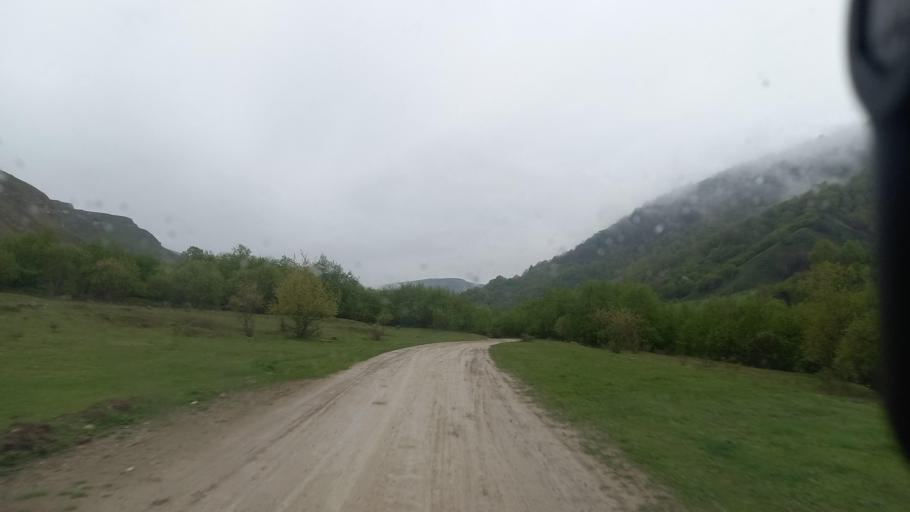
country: RU
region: Kabardino-Balkariya
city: Gundelen
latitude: 43.5983
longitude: 43.0464
